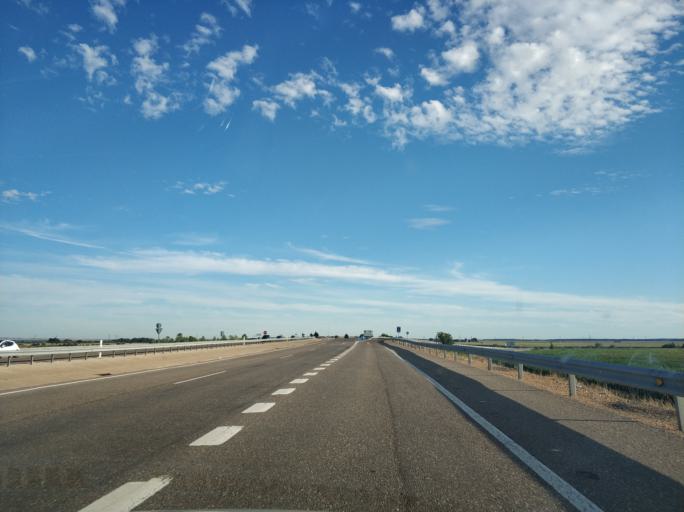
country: ES
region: Castille and Leon
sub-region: Provincia de Leon
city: Villamanan
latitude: 42.3307
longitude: -5.6098
